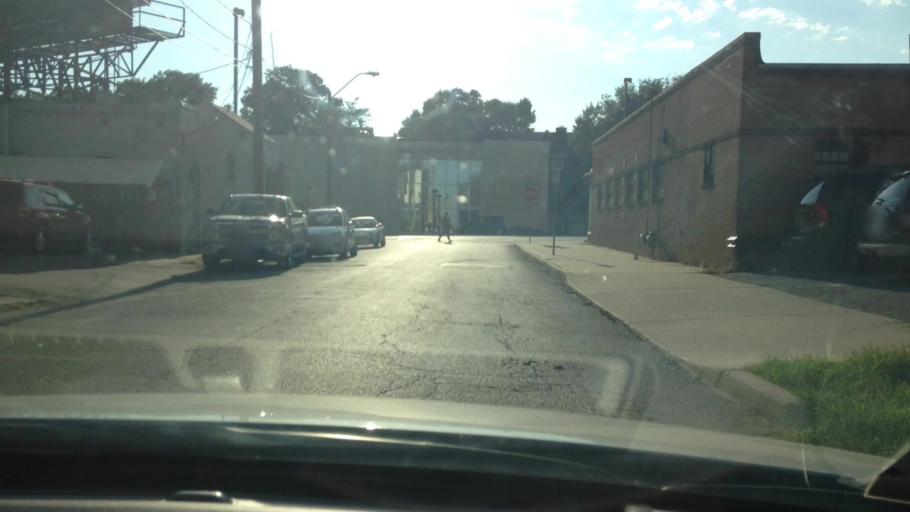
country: US
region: Kansas
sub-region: Johnson County
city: Westwood
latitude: 39.0585
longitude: -94.5898
